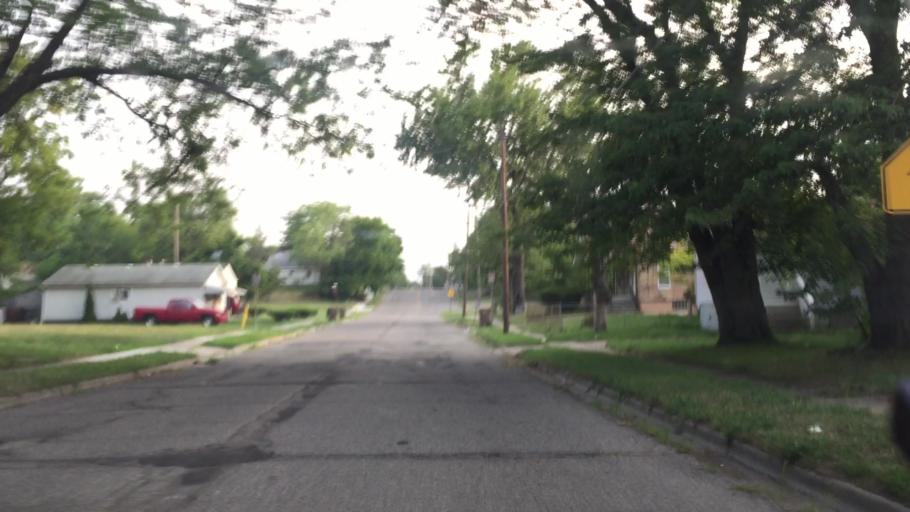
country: US
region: Michigan
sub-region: Oakland County
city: Pontiac
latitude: 42.6357
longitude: -83.2751
